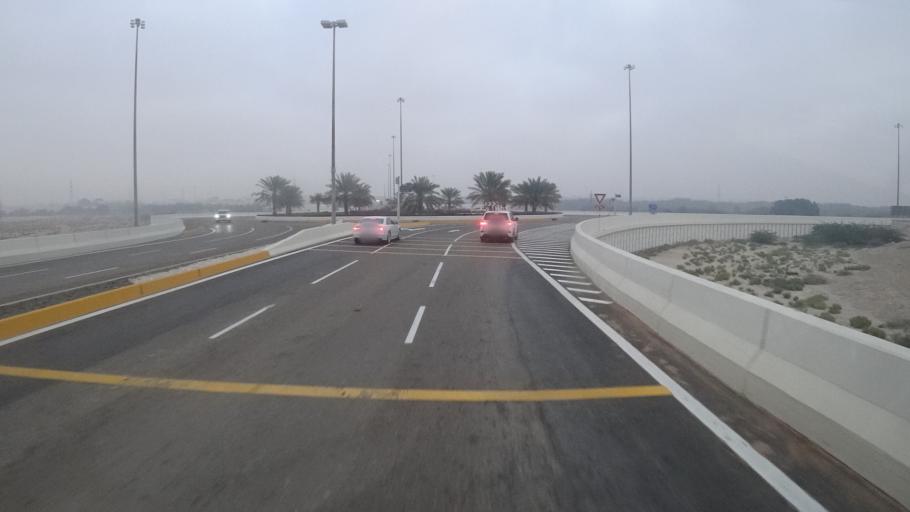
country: AE
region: Abu Dhabi
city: Abu Dhabi
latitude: 24.2466
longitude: 54.7052
